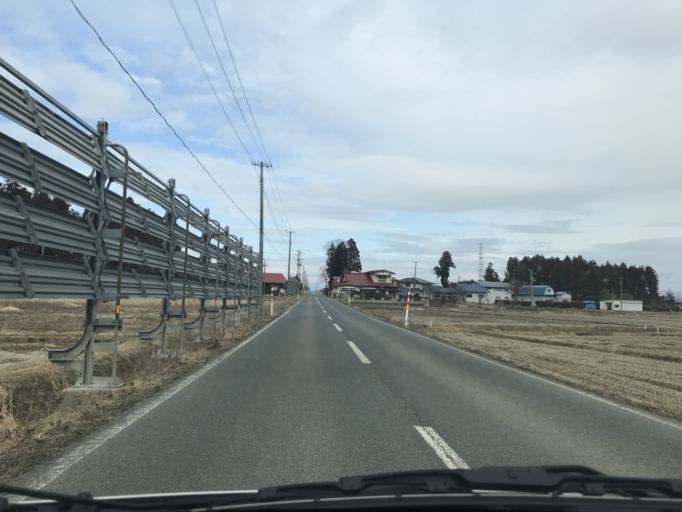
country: JP
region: Iwate
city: Hanamaki
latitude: 39.3383
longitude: 141.0383
